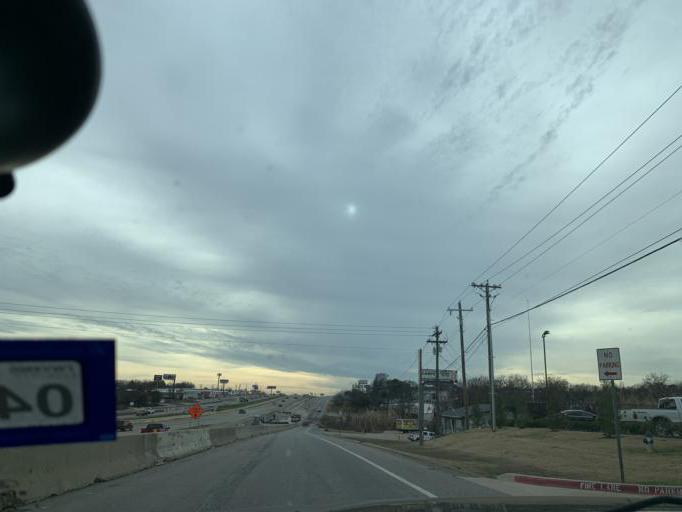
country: US
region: Texas
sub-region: Dallas County
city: Duncanville
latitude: 32.6405
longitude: -96.8928
